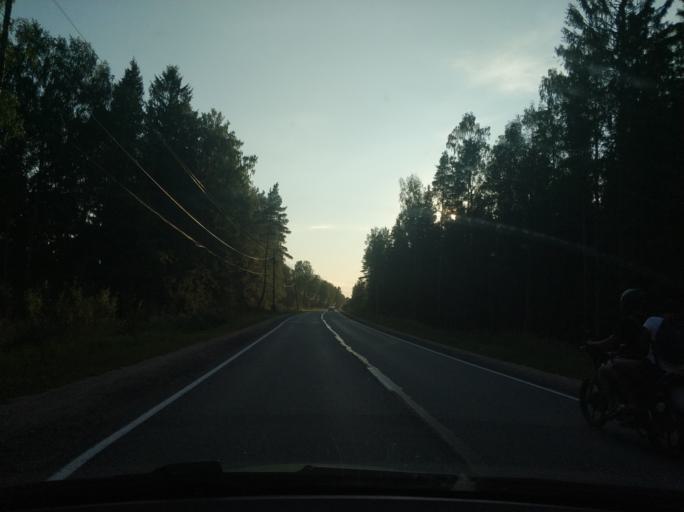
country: RU
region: Leningrad
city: Borisova Griva
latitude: 60.0916
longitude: 30.9991
